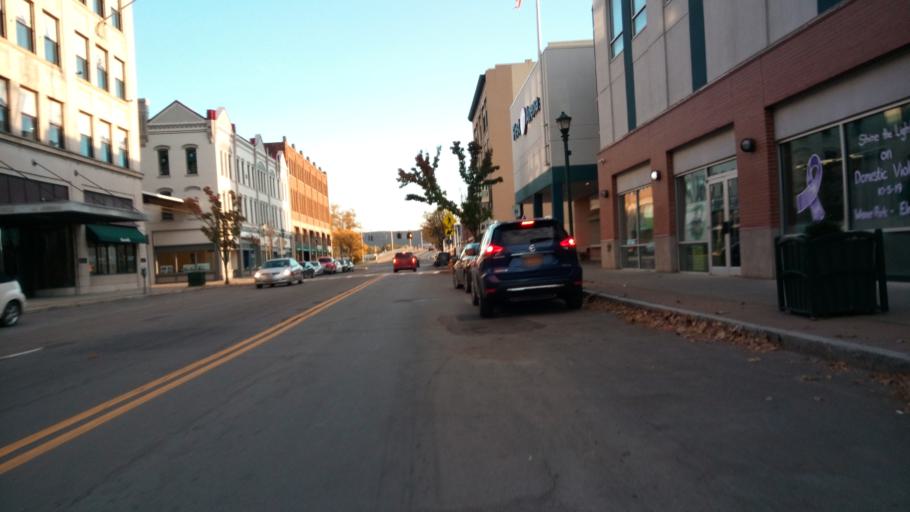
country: US
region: New York
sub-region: Chemung County
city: Elmira
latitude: 42.0887
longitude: -76.8077
